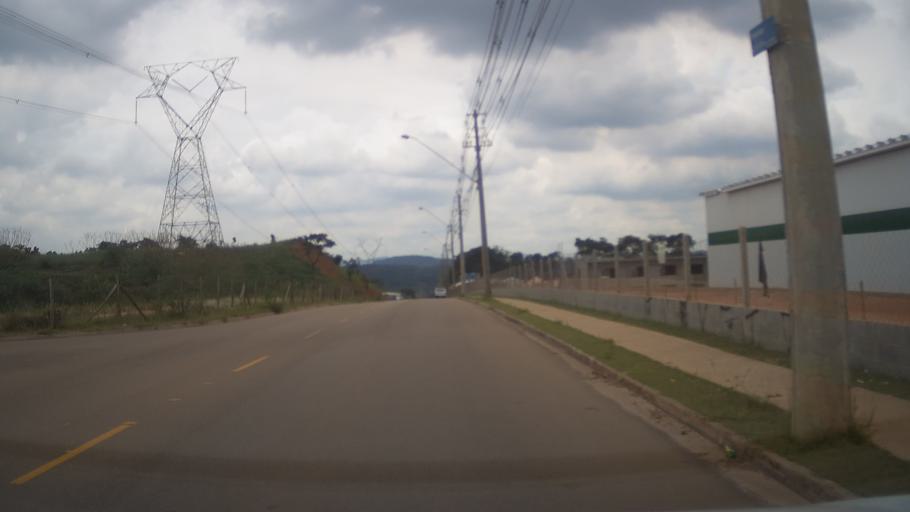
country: BR
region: Sao Paulo
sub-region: Itupeva
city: Itupeva
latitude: -23.1512
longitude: -47.0023
